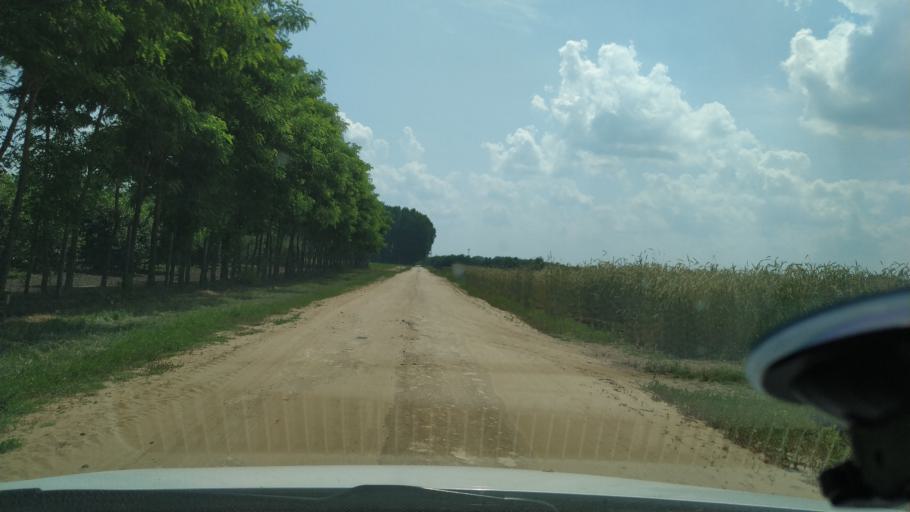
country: HU
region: Pest
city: Szentmartonkata
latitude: 47.4281
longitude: 19.7076
